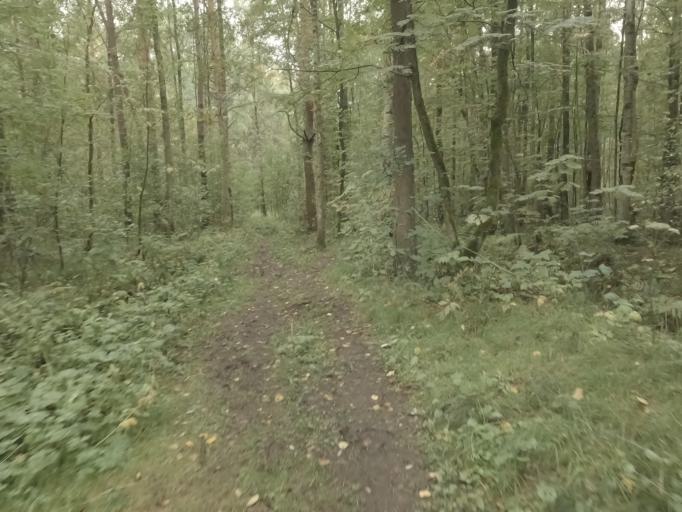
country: RU
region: St.-Petersburg
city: Krasnogvargeisky
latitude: 59.9636
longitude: 30.5039
